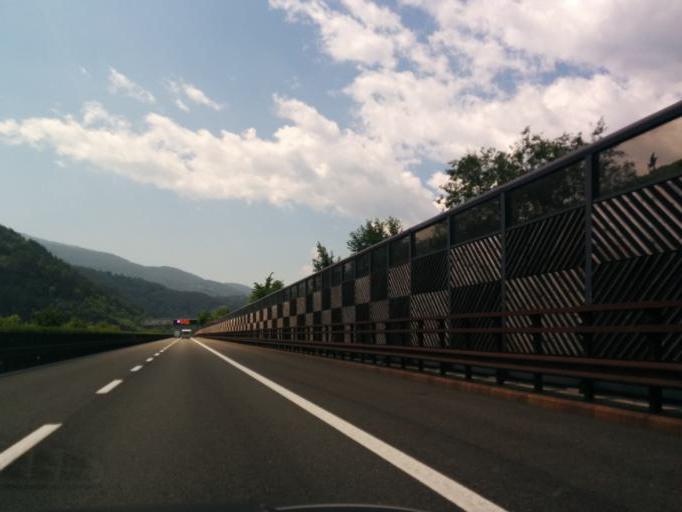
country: IT
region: Trentino-Alto Adige
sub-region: Bolzano
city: Velturno
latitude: 46.6717
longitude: 11.6179
